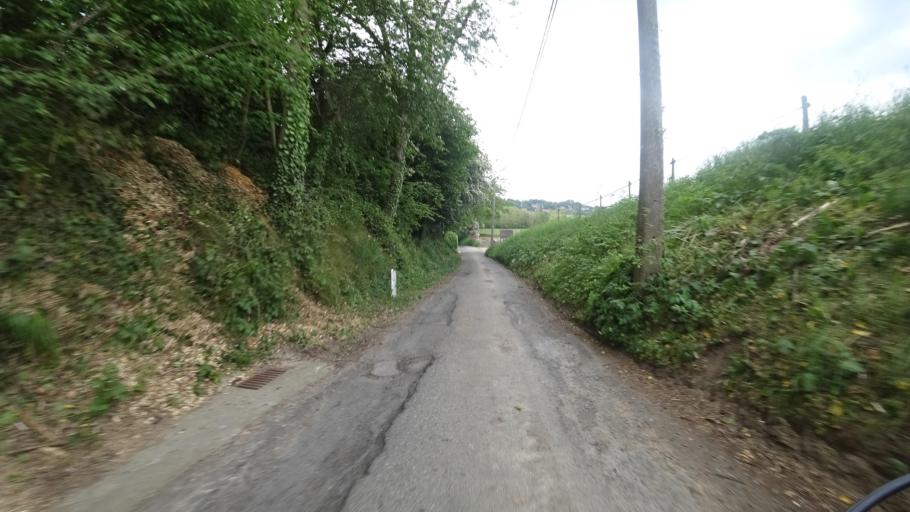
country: BE
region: Wallonia
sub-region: Province du Brabant Wallon
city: Grez-Doiceau
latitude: 50.7168
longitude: 4.6904
